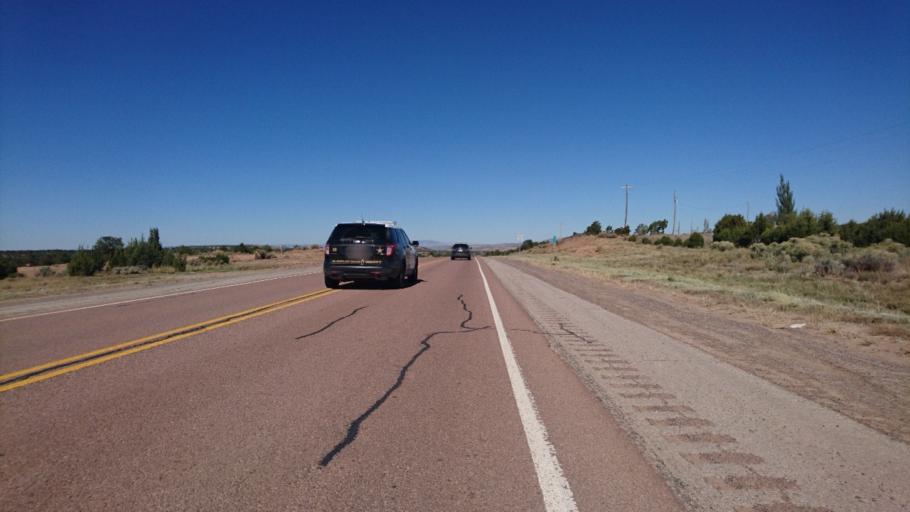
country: US
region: New Mexico
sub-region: McKinley County
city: Gallup
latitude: 35.3835
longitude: -108.7535
